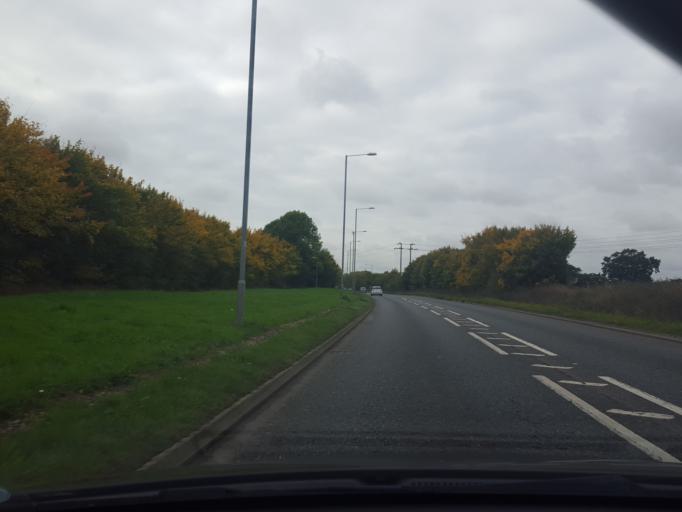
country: GB
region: England
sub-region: Essex
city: Little Clacton
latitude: 51.8195
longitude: 1.1566
